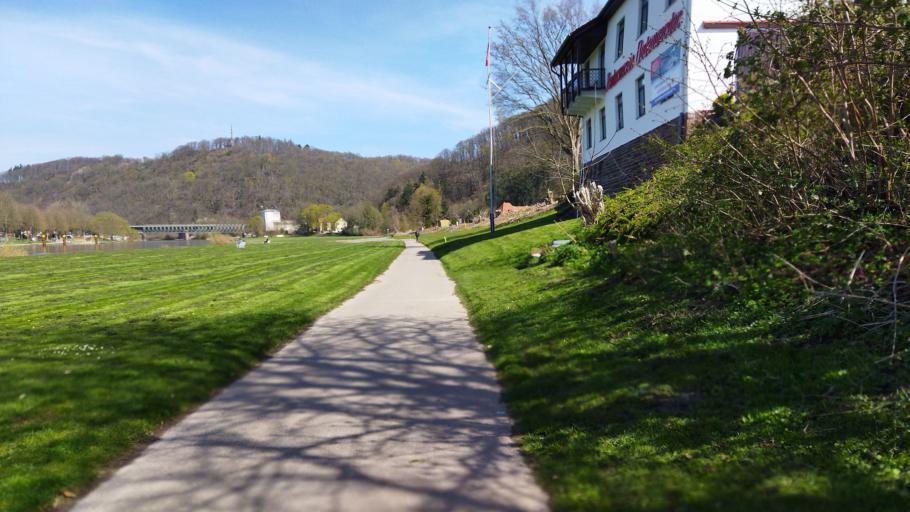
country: DE
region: Lower Saxony
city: Bodenwerder
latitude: 51.9762
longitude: 9.5188
